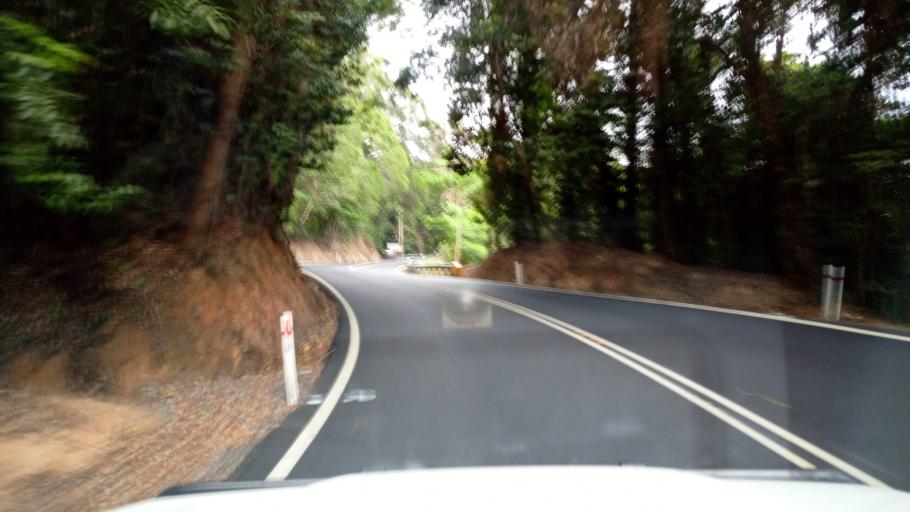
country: AU
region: Queensland
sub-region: Tablelands
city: Kuranda
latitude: -16.8328
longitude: 145.6701
